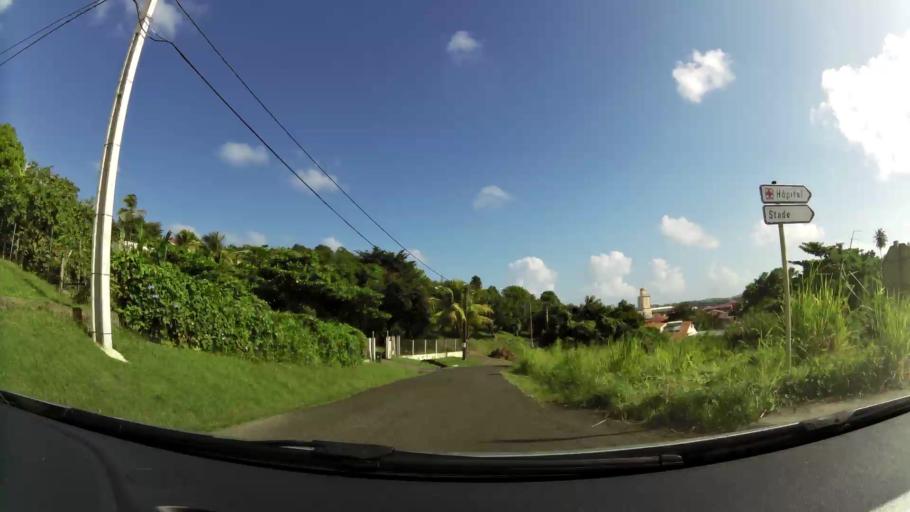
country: MQ
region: Martinique
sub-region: Martinique
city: La Trinite
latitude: 14.7385
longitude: -60.9663
